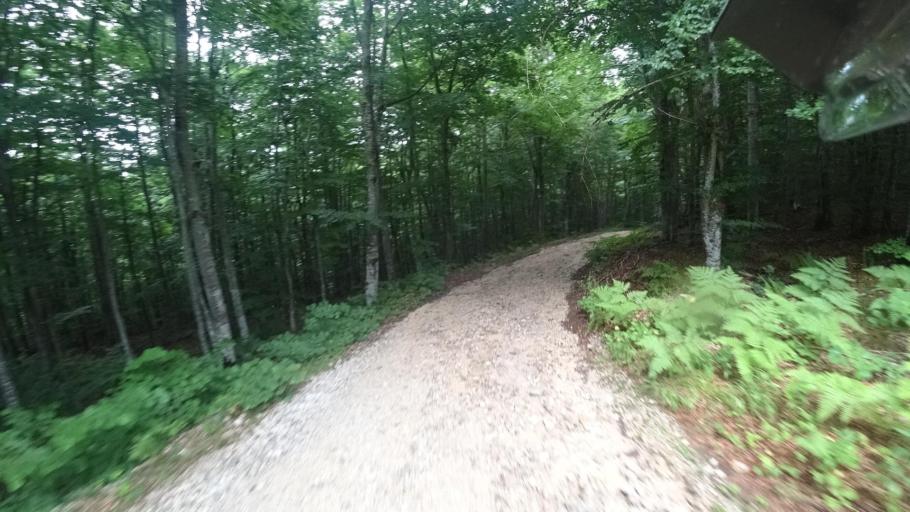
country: HR
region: Licko-Senjska
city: Jezerce
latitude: 44.7479
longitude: 15.6296
